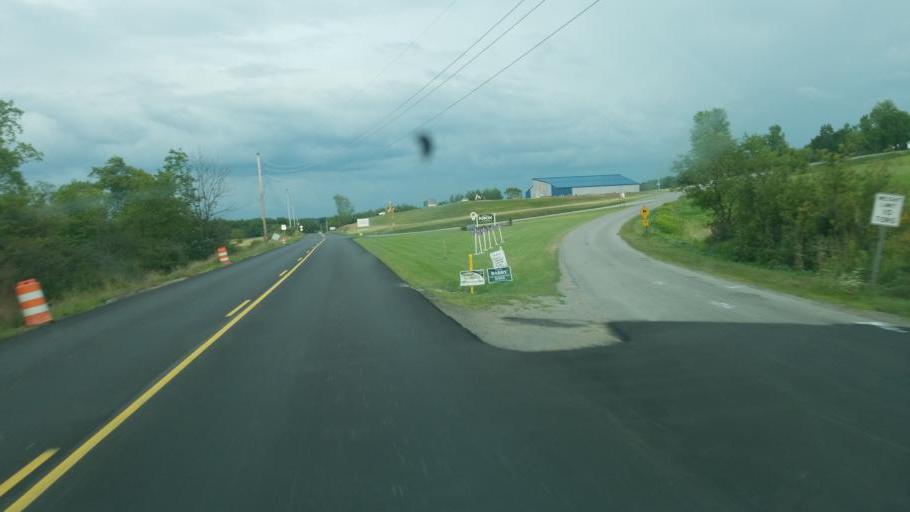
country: US
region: Pennsylvania
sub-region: Clarion County
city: Knox
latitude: 41.2425
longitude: -79.5356
